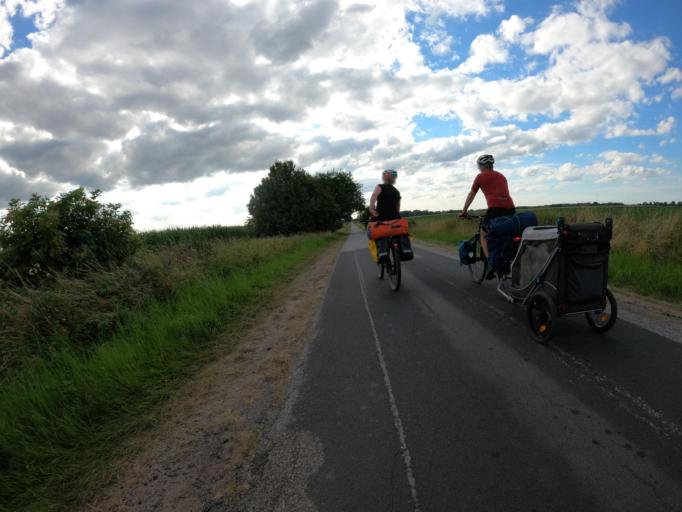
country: PL
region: West Pomeranian Voivodeship
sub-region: Powiat swidwinski
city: Swidwin
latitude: 53.7589
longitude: 15.6590
